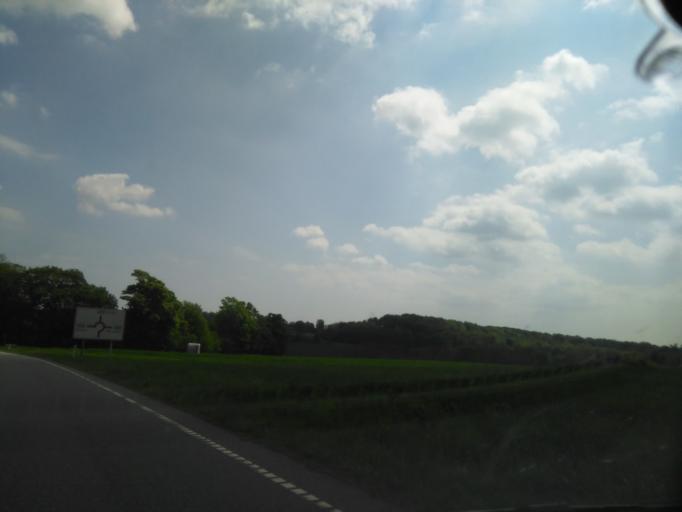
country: DK
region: Central Jutland
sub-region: Skanderborg Kommune
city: Stilling
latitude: 55.9935
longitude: 10.0190
